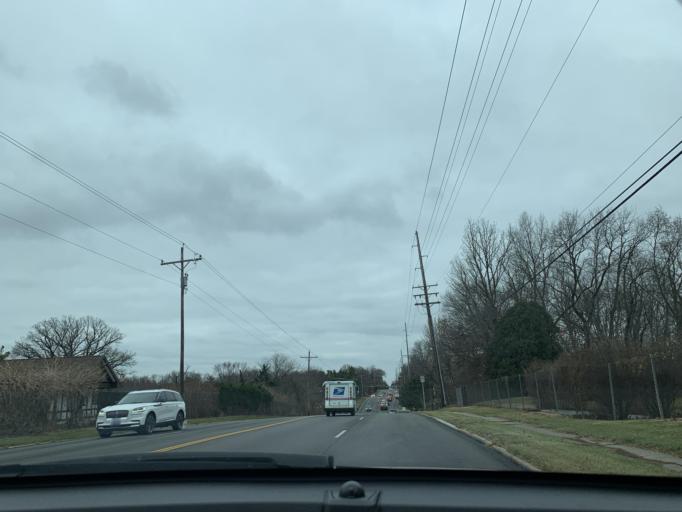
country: US
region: Illinois
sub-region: Sangamon County
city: Leland Grove
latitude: 39.7834
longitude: -89.6870
